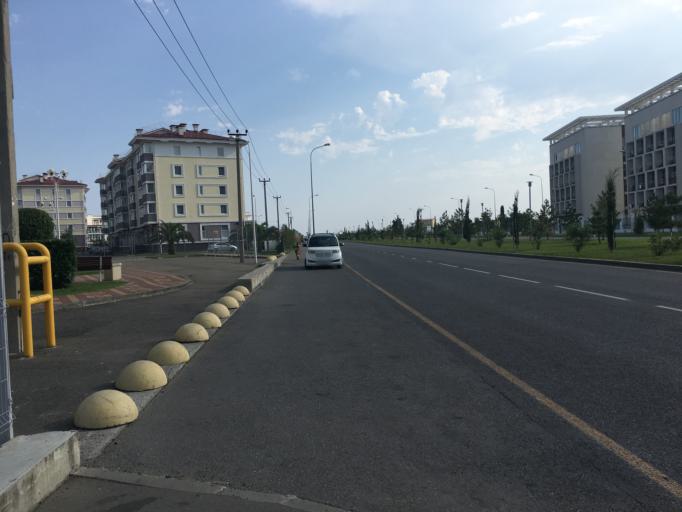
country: RU
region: Krasnodarskiy
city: Vysokoye
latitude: 43.3900
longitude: 39.9909
